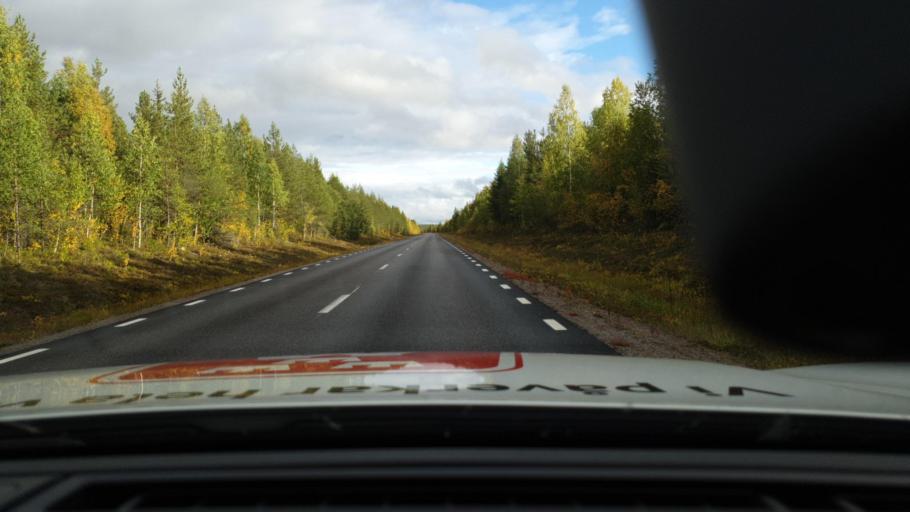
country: SE
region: Norrbotten
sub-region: Overkalix Kommun
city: OEverkalix
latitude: 66.9982
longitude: 22.5661
